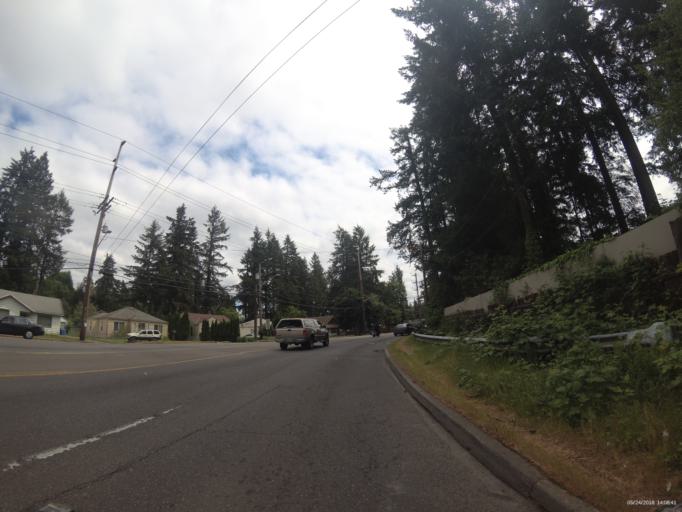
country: US
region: Washington
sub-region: Pierce County
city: Lakewood
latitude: 47.1407
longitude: -122.5262
